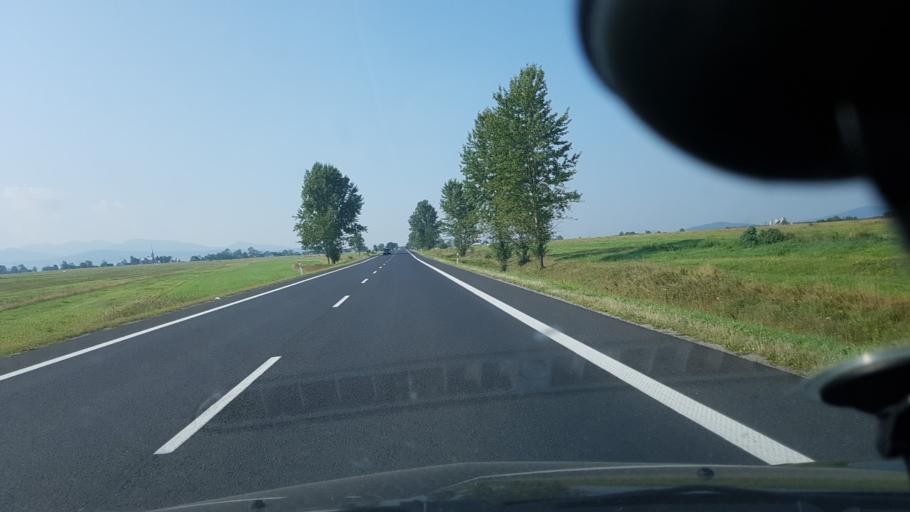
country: PL
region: Lesser Poland Voivodeship
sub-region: Powiat nowotarski
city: Chyzne
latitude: 49.4363
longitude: 19.6798
